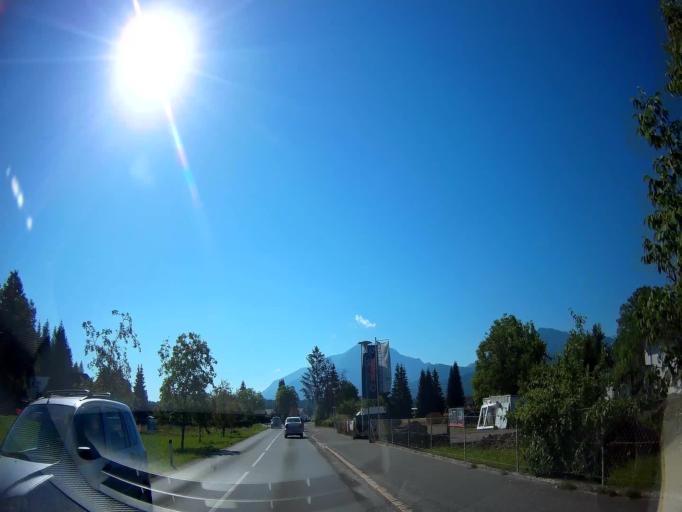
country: AT
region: Carinthia
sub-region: Politischer Bezirk Volkermarkt
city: Eberndorf
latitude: 46.5872
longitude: 14.6475
